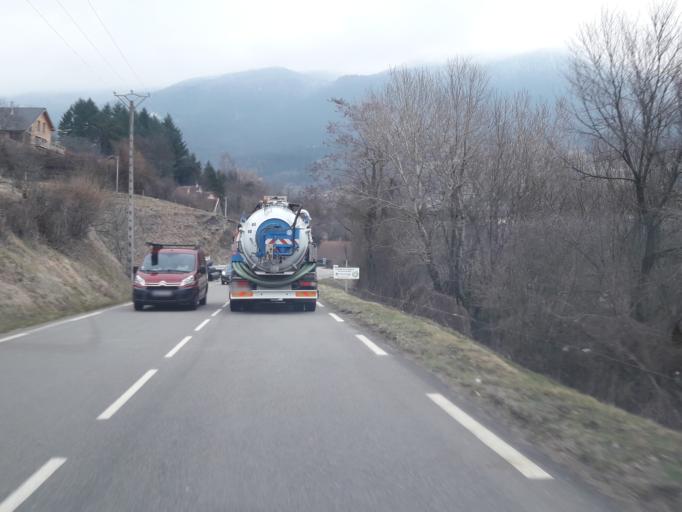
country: FR
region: Rhone-Alpes
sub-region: Departement de l'Isere
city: Theys
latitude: 45.3043
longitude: 5.9883
